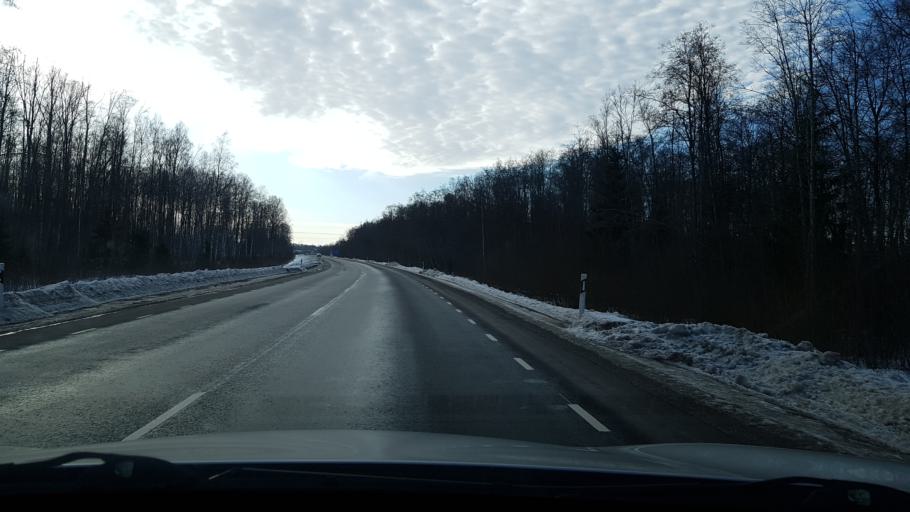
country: EE
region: Viljandimaa
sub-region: Viljandi linn
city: Viljandi
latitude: 58.3835
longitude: 25.5599
